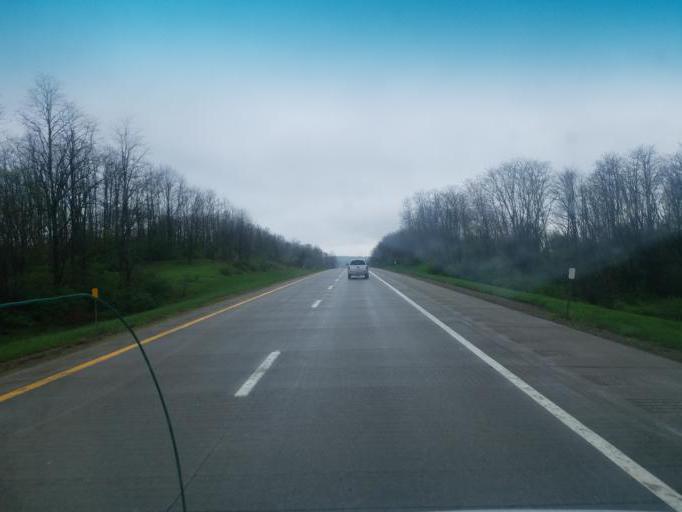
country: US
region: New York
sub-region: Chautauqua County
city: Clymer
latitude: 42.1476
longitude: -79.6359
